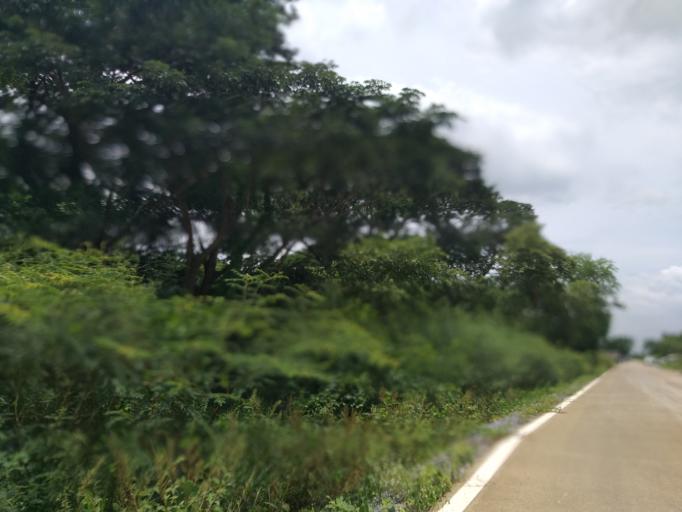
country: TH
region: Pathum Thani
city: Ban Lam Luk Ka
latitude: 13.9828
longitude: 100.8532
